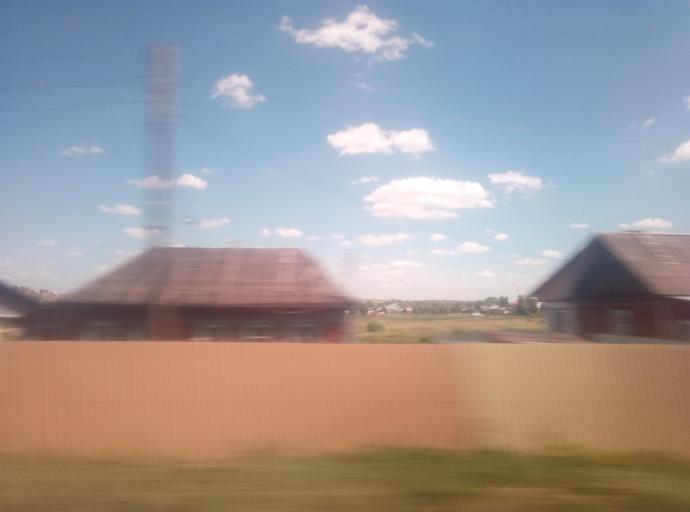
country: RU
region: Tula
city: Kireyevsk
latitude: 53.9688
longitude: 37.9327
